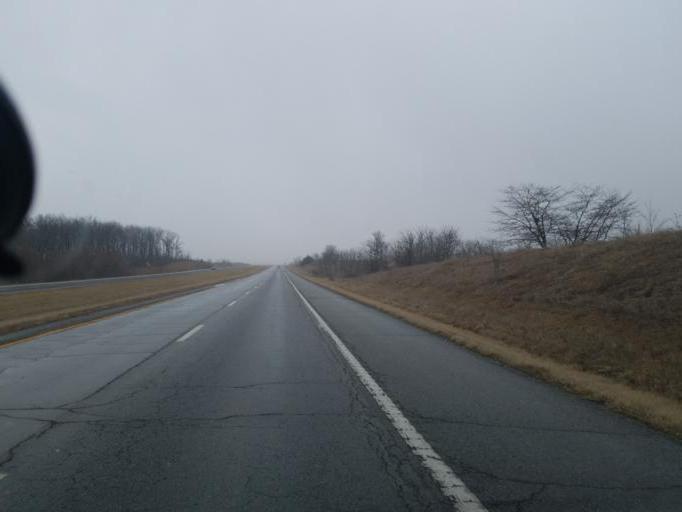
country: US
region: Missouri
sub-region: Macon County
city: La Plata
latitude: 39.9937
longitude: -92.4757
